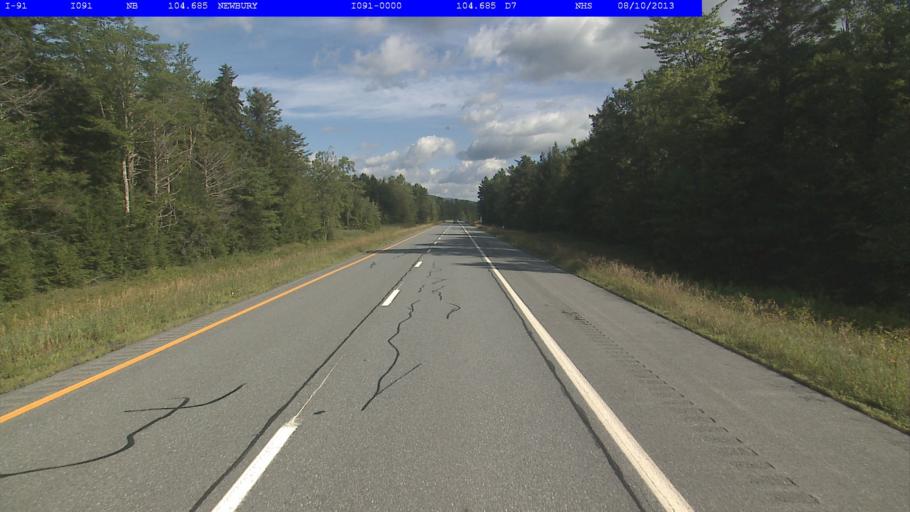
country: US
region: New Hampshire
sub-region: Grafton County
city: Haverhill
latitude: 44.0808
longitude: -72.1119
